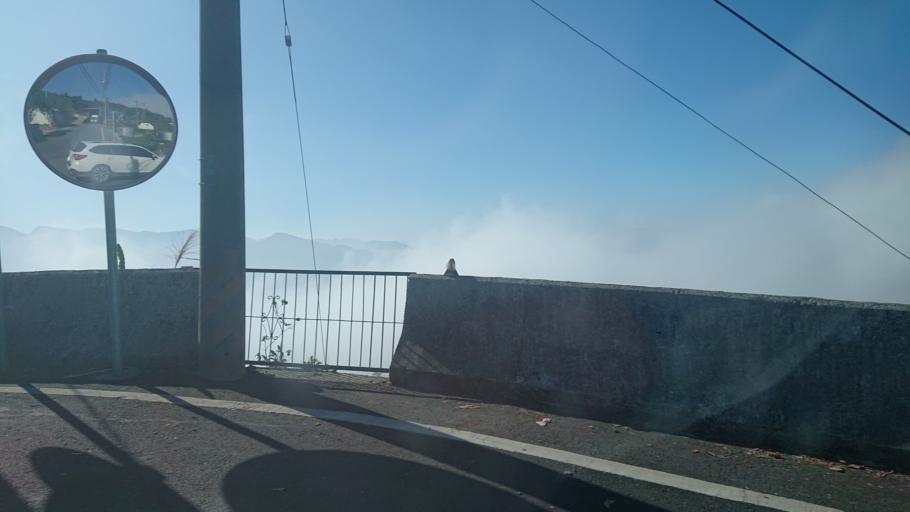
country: TW
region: Taiwan
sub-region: Chiayi
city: Jiayi Shi
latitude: 23.4773
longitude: 120.6990
